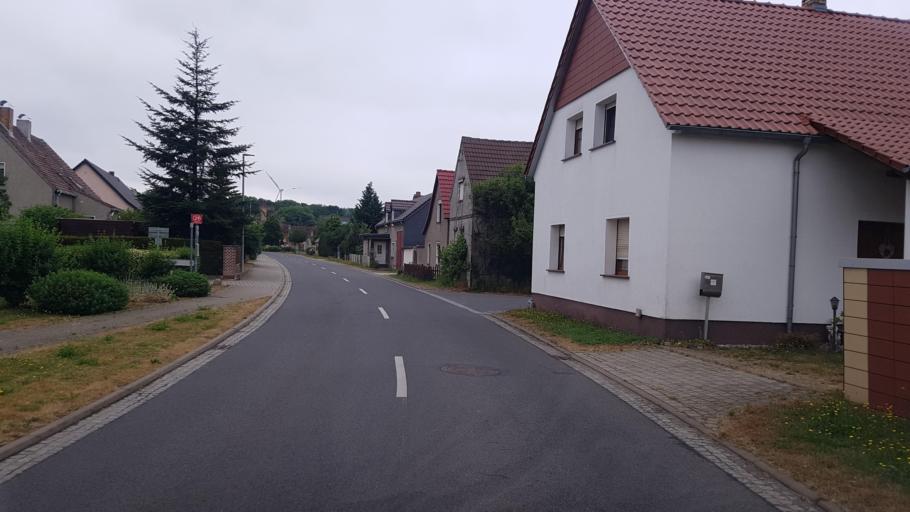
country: DE
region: Brandenburg
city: Schwarzbach
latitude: 51.4728
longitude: 13.9428
